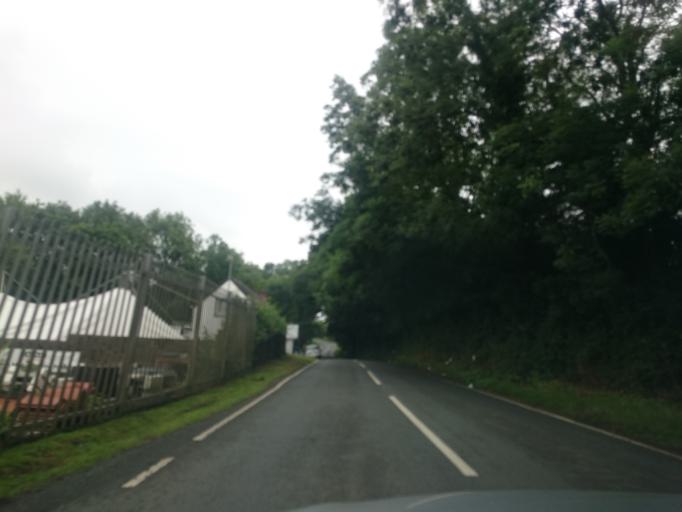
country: GB
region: Wales
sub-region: Pembrokeshire
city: Freystrop
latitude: 51.7697
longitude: -4.9625
